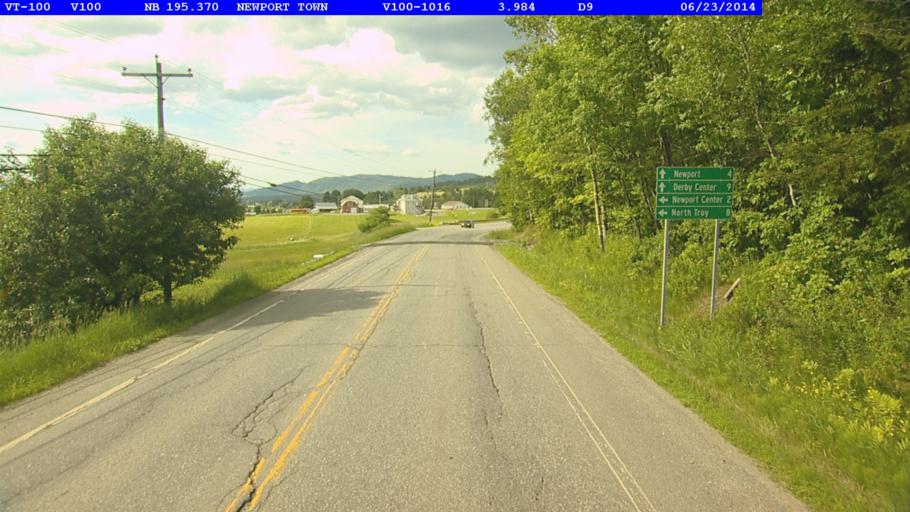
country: US
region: Vermont
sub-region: Orleans County
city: Newport
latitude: 44.9283
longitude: -72.2881
